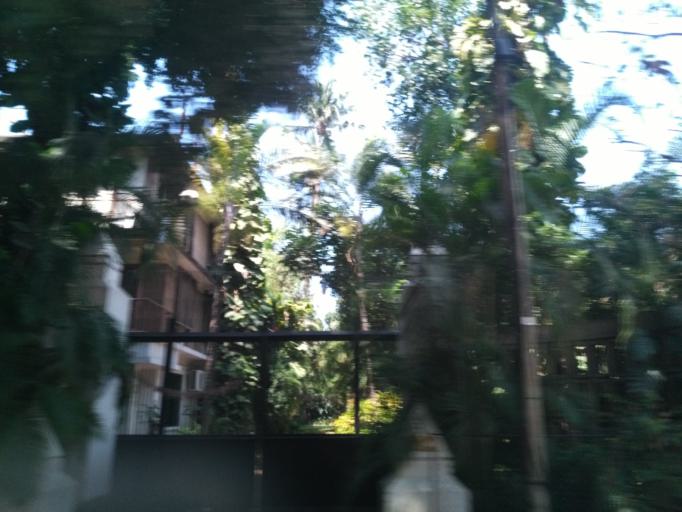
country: TZ
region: Dar es Salaam
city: Dar es Salaam
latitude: -6.8063
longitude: 39.2822
